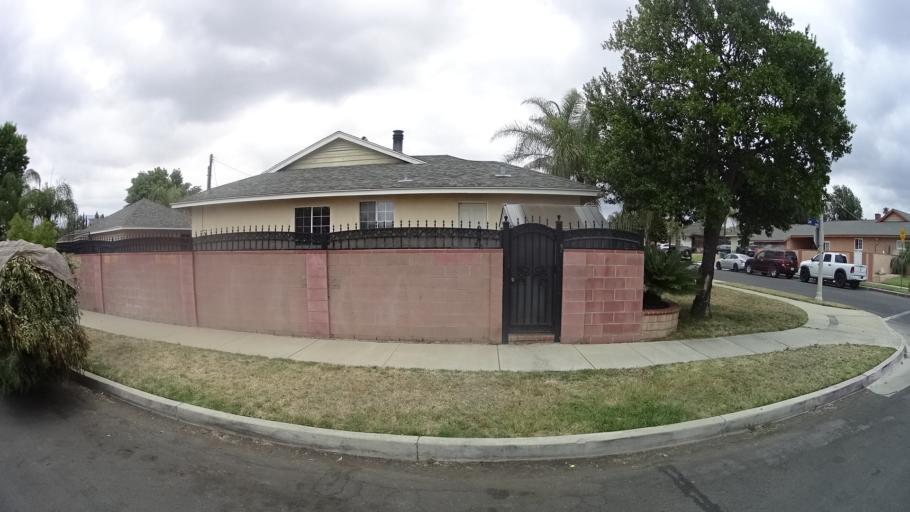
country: US
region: California
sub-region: Los Angeles County
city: San Fernando
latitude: 34.2639
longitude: -118.4477
